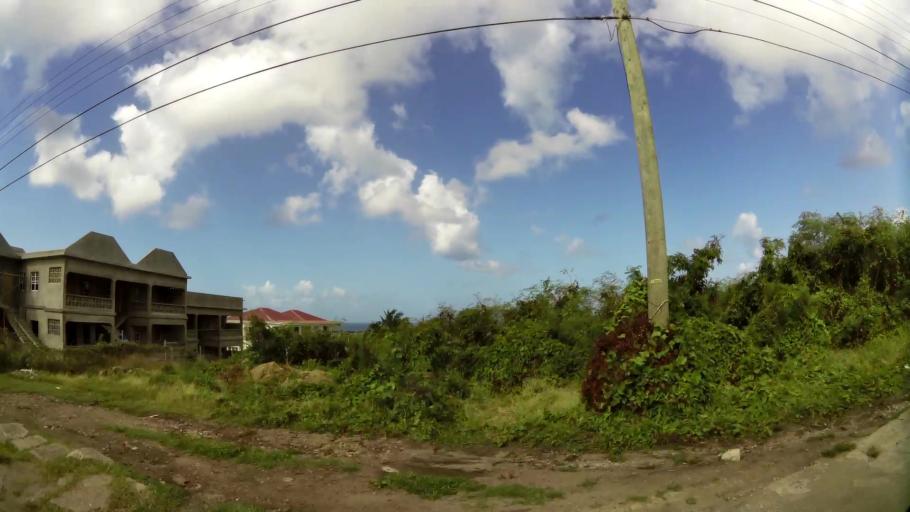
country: KN
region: Saint Paul Charlestown
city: Charlestown
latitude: 17.1323
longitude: -62.6131
